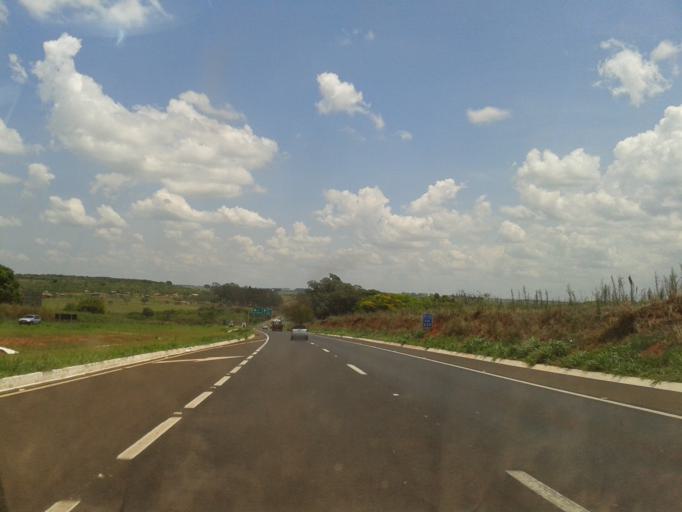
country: BR
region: Minas Gerais
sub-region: Uberlandia
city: Uberlandia
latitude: -18.8904
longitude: -48.4309
